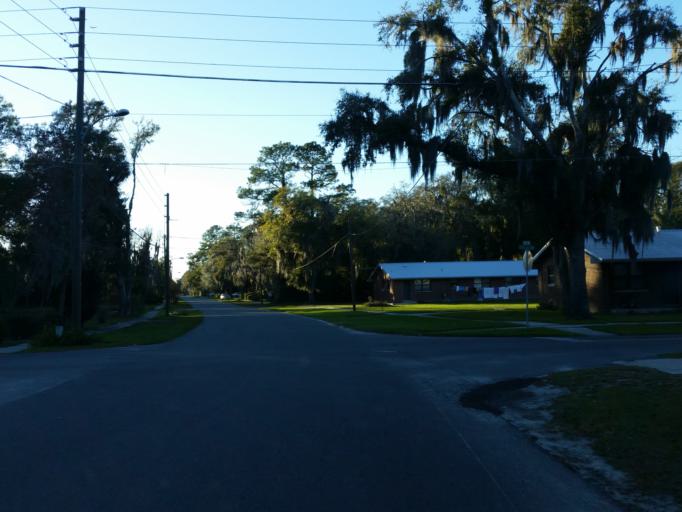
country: US
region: Florida
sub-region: Hamilton County
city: Jasper
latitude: 30.5209
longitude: -82.9479
